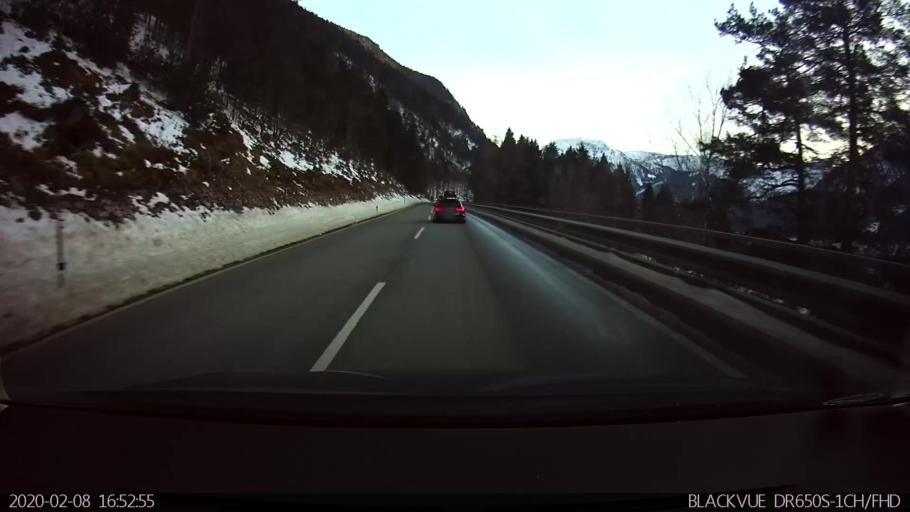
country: AT
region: Tyrol
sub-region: Politischer Bezirk Schwaz
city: Achenkirch
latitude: 47.4714
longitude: 11.7141
